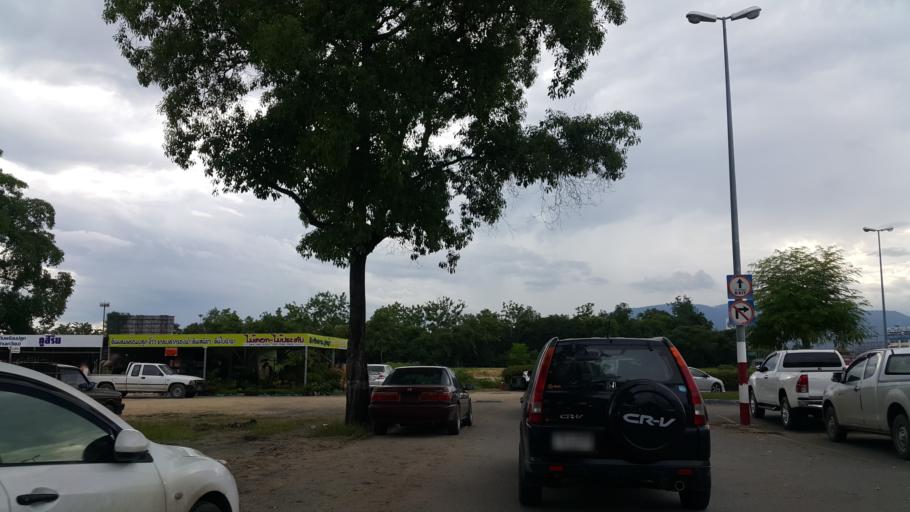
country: TH
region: Chiang Mai
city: Chiang Mai
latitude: 18.7678
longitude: 99.0327
